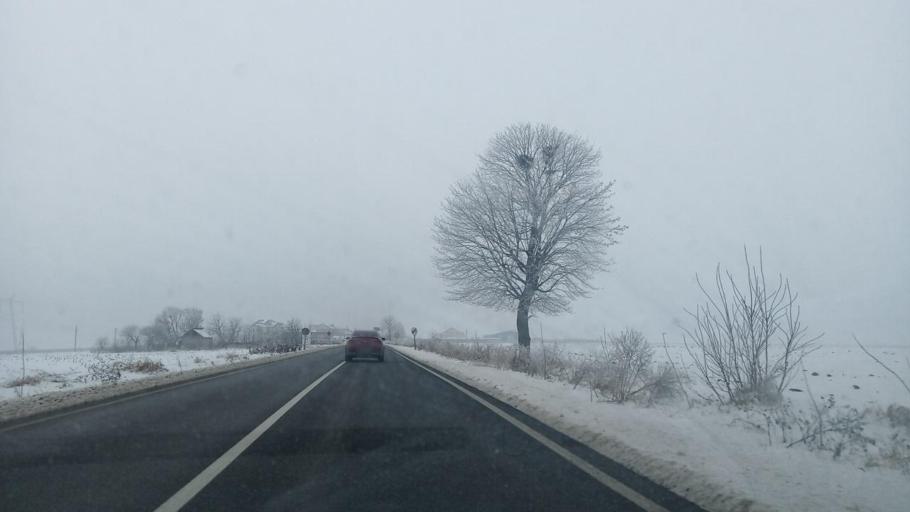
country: RO
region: Neamt
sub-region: Comuna Botesti
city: Nisiporesti
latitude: 47.0948
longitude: 26.7038
